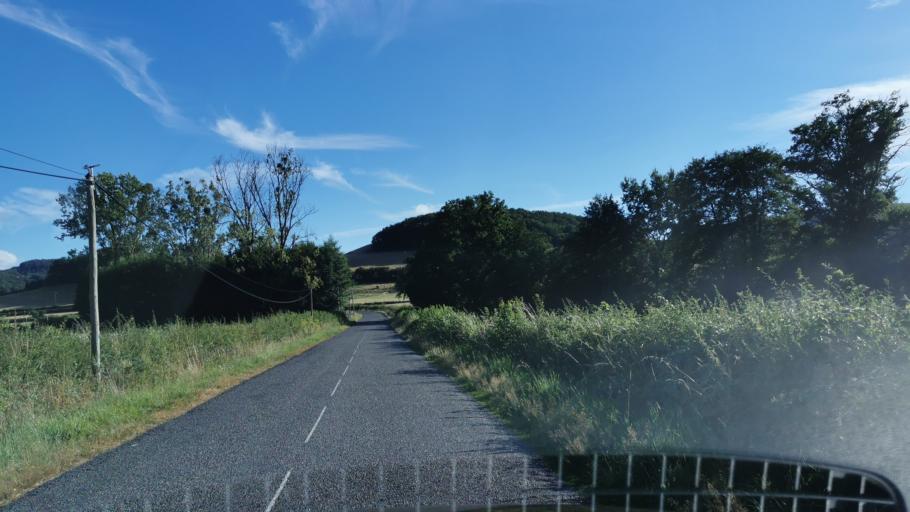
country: FR
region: Bourgogne
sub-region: Departement de Saone-et-Loire
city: Marmagne
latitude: 46.8147
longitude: 4.3281
